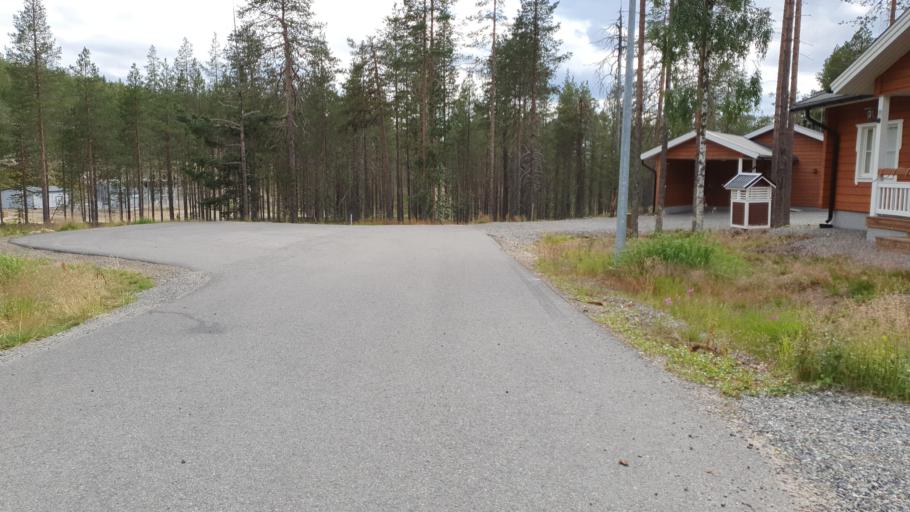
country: FI
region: Lapland
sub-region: Tunturi-Lappi
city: Kolari
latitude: 67.5933
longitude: 24.1219
